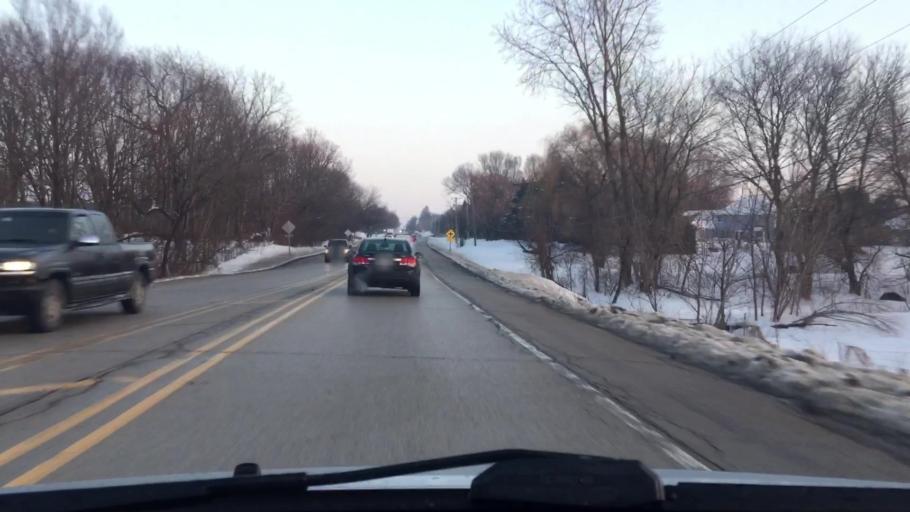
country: US
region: Illinois
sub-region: Kane County
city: Village of Campton Hills
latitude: 41.9319
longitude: -88.3812
